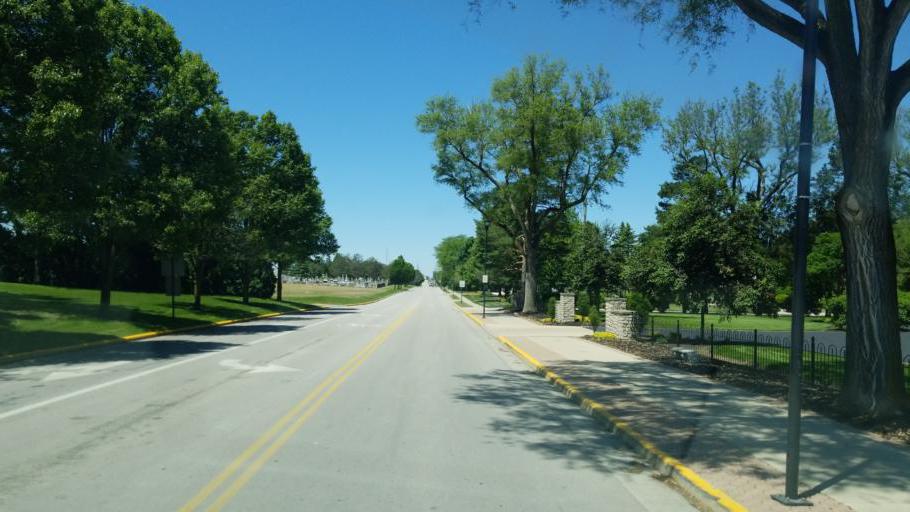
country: US
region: Ohio
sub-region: Auglaize County
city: Minster
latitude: 40.3858
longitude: -84.3768
